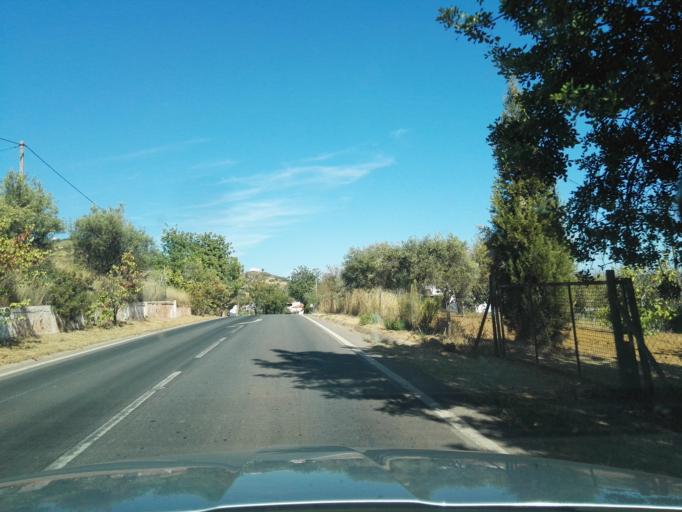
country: PT
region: Faro
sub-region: Olhao
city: Moncarapacho
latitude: 37.1524
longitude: -7.8014
